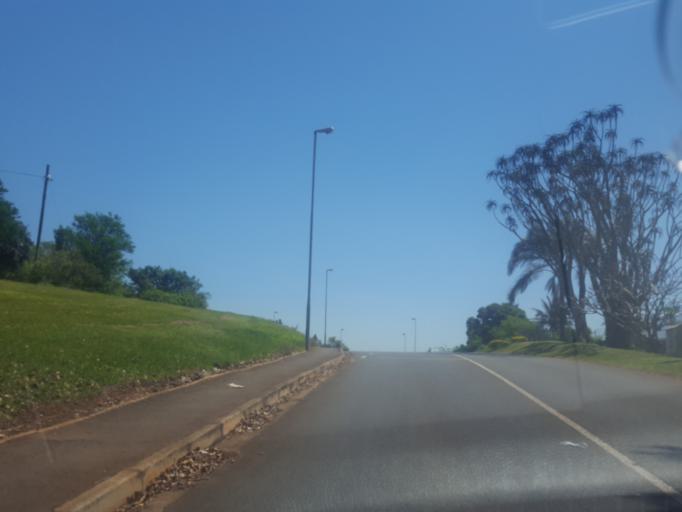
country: ZA
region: KwaZulu-Natal
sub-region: uThungulu District Municipality
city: Empangeni
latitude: -28.7423
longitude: 31.9020
